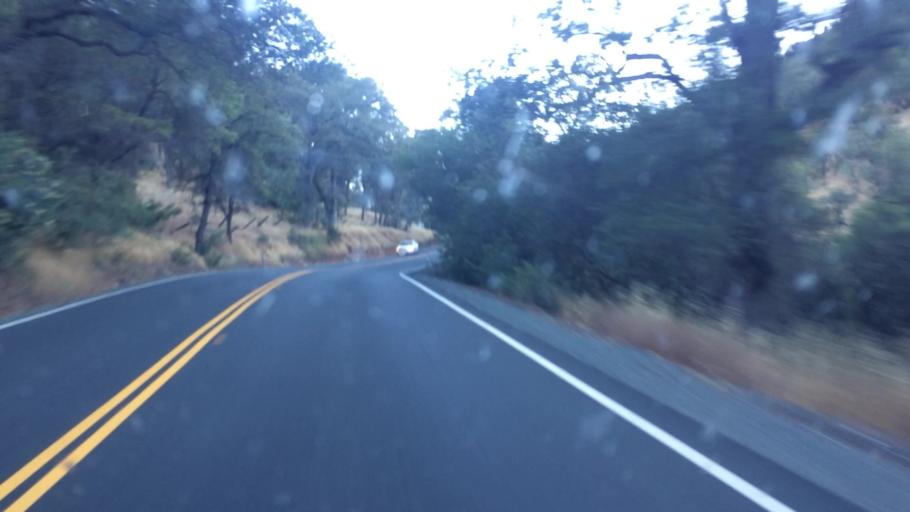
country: US
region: California
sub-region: El Dorado County
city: Deer Park
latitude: 38.6078
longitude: -120.8533
